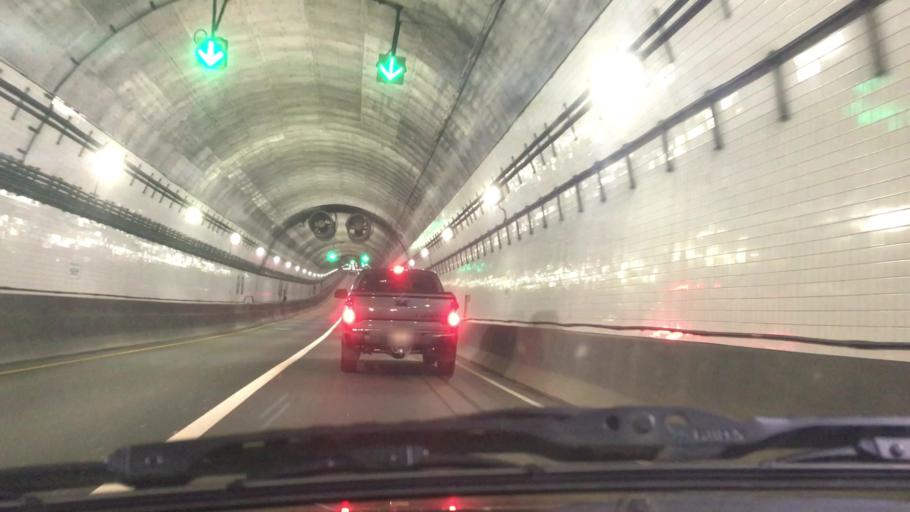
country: US
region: Virginia
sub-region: City of Portsmouth
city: Portsmouth
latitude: 36.8333
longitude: -76.2964
